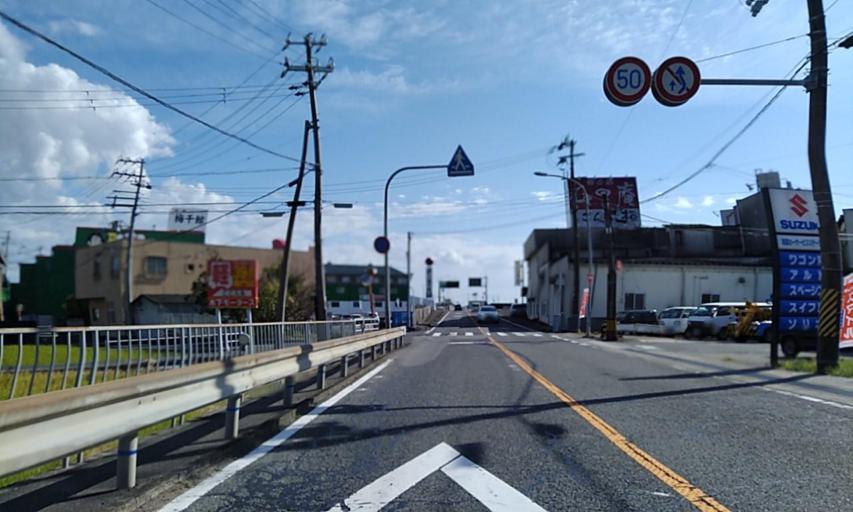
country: JP
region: Wakayama
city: Tanabe
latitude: 33.7734
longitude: 135.3129
